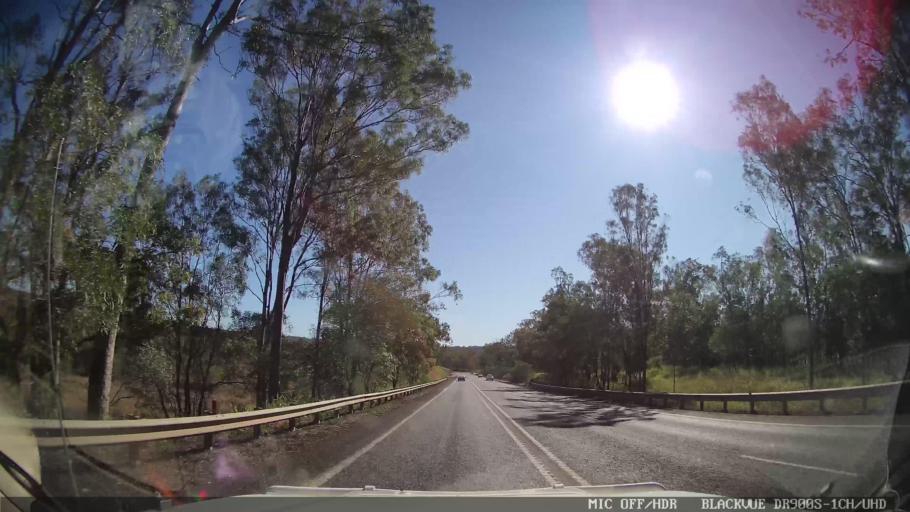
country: AU
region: Queensland
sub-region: Bundaberg
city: Childers
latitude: -25.2337
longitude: 152.2468
